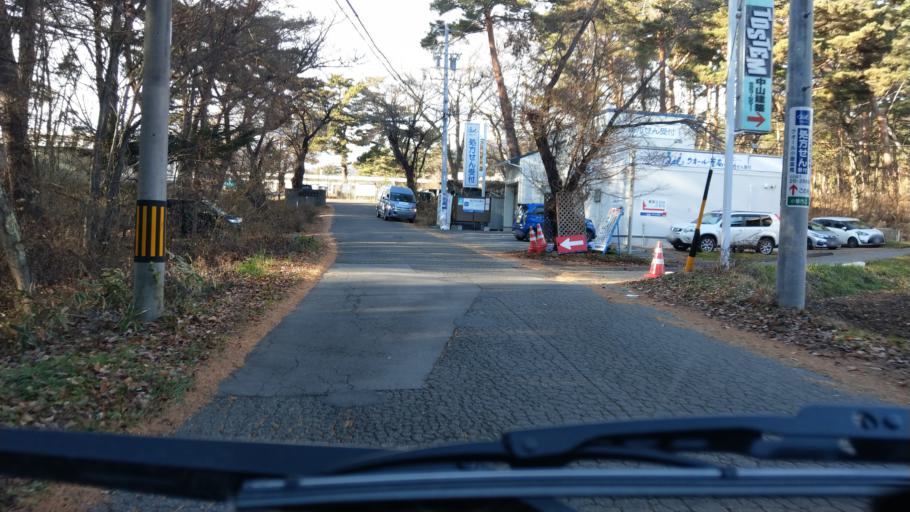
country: JP
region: Nagano
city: Komoro
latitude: 36.3454
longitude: 138.4523
